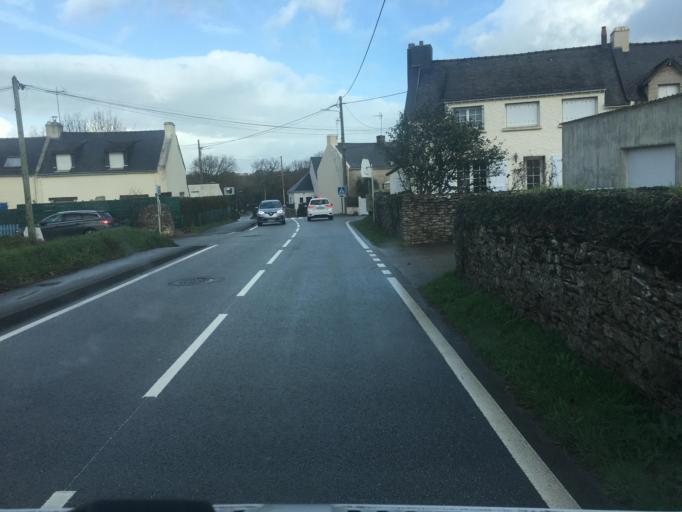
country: FR
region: Brittany
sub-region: Departement du Morbihan
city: Sarzeau
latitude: 47.5138
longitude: -2.7665
